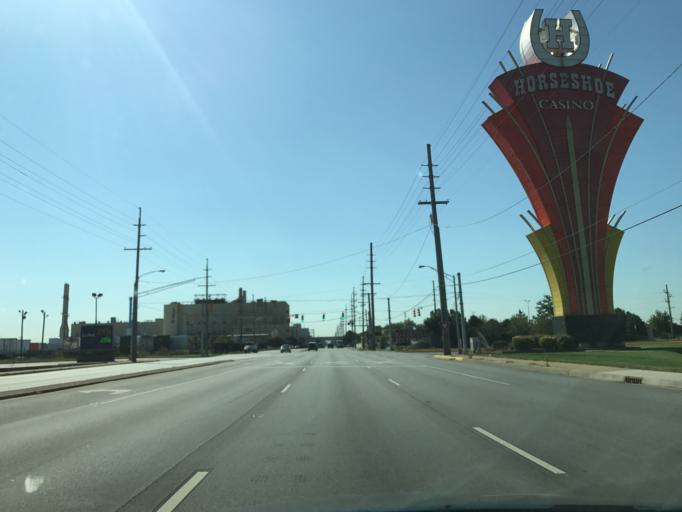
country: US
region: Indiana
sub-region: Lake County
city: Whiting
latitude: 41.6943
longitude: -87.5153
